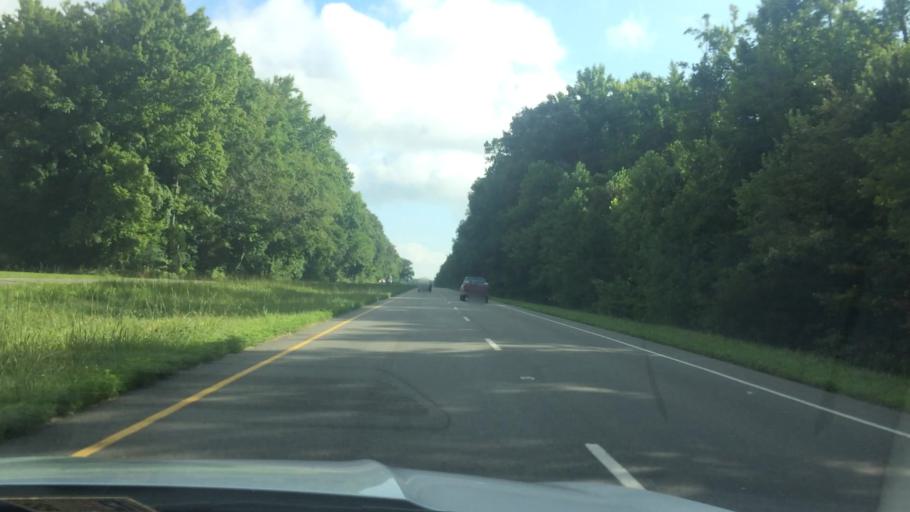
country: US
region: Virginia
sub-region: Gloucester County
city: Gloucester Courthouse
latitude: 37.4297
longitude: -76.4818
